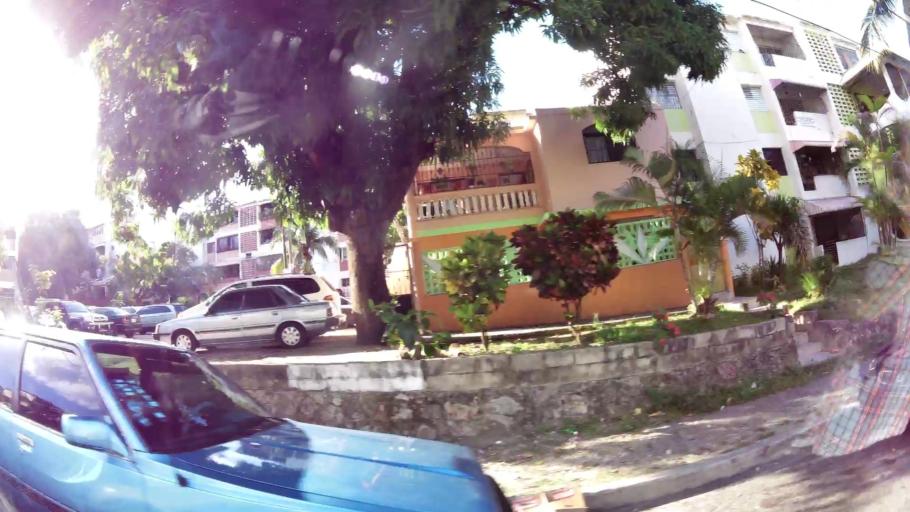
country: DO
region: Nacional
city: Santo Domingo
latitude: 18.4976
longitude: -69.9655
